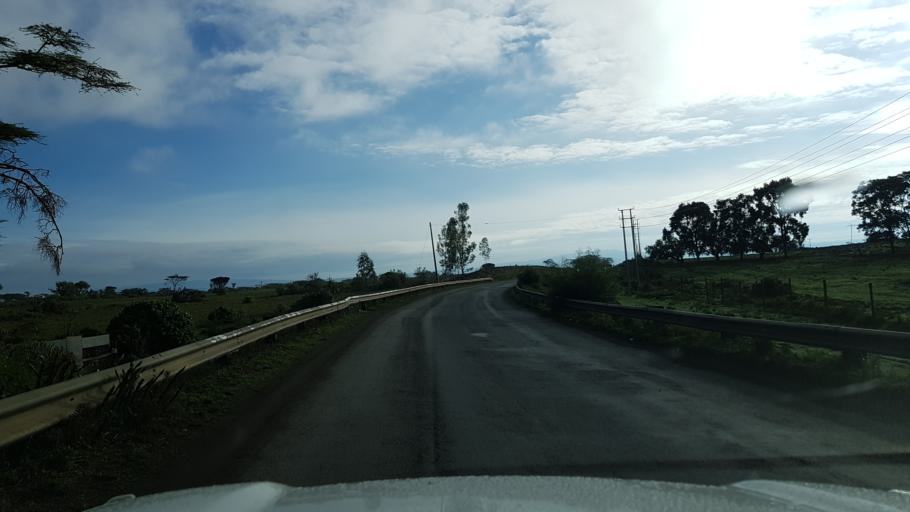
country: KE
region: Nakuru
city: Naivasha
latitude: -0.8215
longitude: 36.3855
